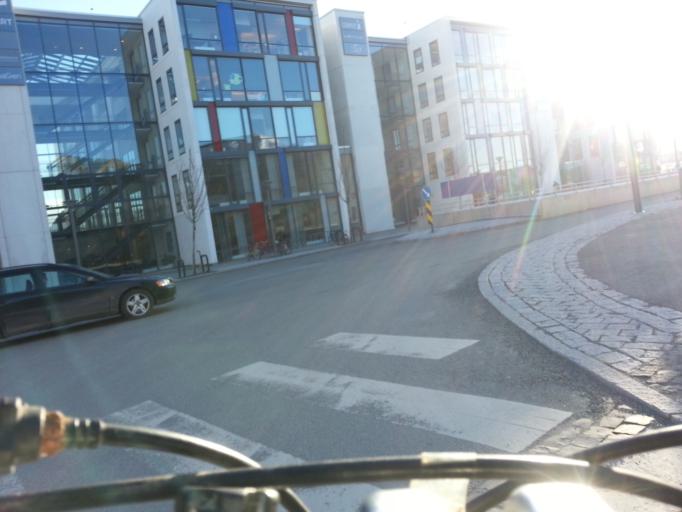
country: NO
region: Sor-Trondelag
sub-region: Trondheim
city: Trondheim
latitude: 63.4406
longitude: 10.4025
